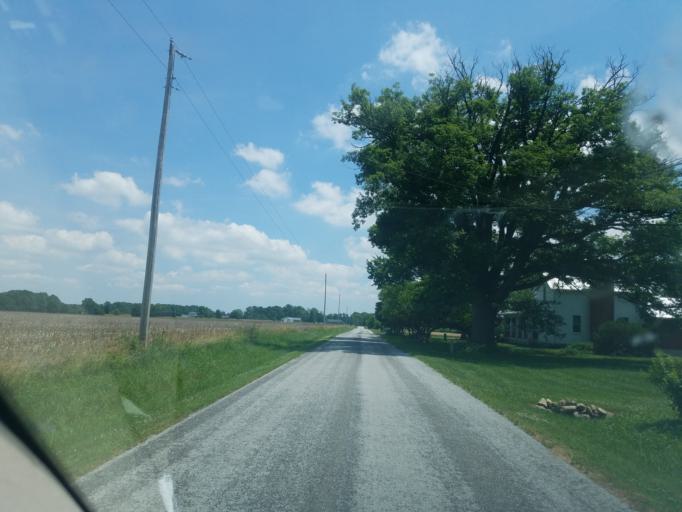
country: US
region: Ohio
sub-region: Hardin County
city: Forest
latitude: 40.7751
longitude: -83.6126
